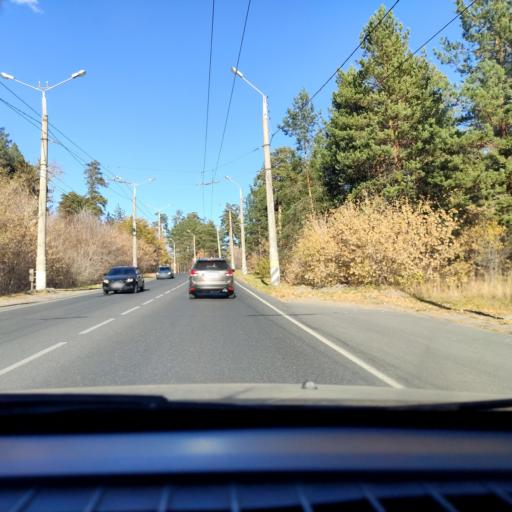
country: RU
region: Samara
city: Tol'yatti
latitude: 53.4767
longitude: 49.3491
